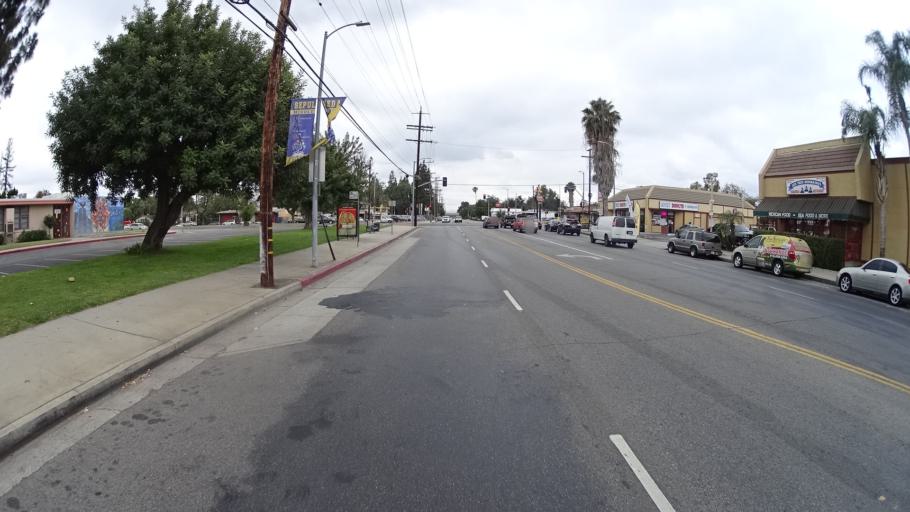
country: US
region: California
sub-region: Los Angeles County
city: San Fernando
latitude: 34.2427
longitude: -118.4666
